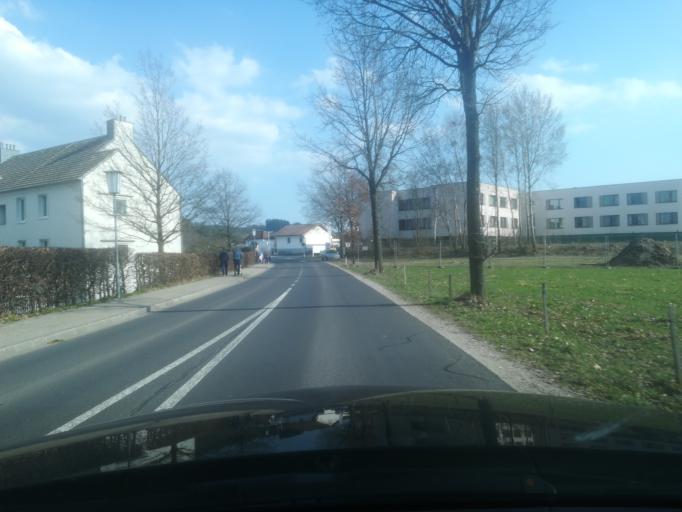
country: AT
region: Upper Austria
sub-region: Politischer Bezirk Perg
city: Perg
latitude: 48.3524
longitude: 14.6658
